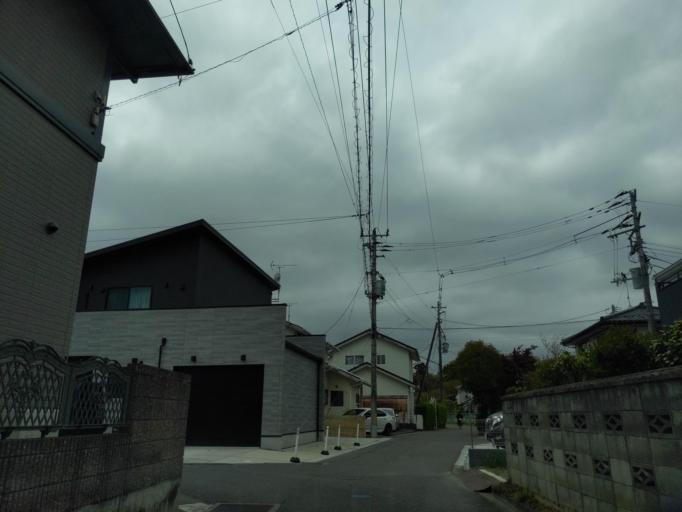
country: JP
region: Fukushima
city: Koriyama
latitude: 37.3808
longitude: 140.3520
